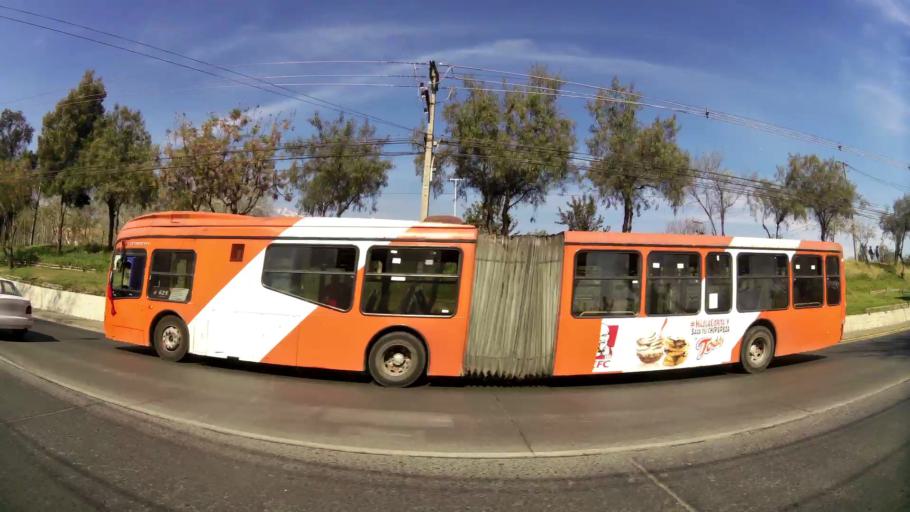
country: CL
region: Santiago Metropolitan
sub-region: Provincia de Santiago
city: Villa Presidente Frei, Nunoa, Santiago, Chile
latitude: -33.4761
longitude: -70.5563
